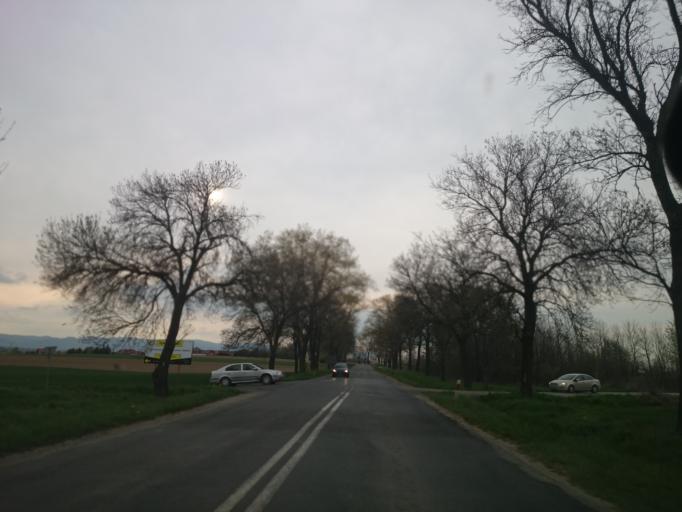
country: PL
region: Lower Silesian Voivodeship
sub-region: Powiat zabkowicki
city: Zabkowice Slaskie
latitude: 50.5866
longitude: 16.8397
